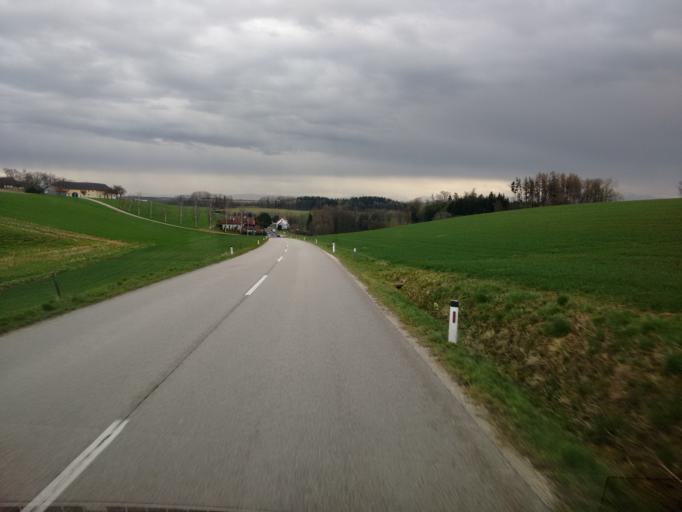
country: AT
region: Upper Austria
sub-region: Politischer Bezirk Linz-Land
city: Horsching
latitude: 48.1475
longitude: 14.2026
